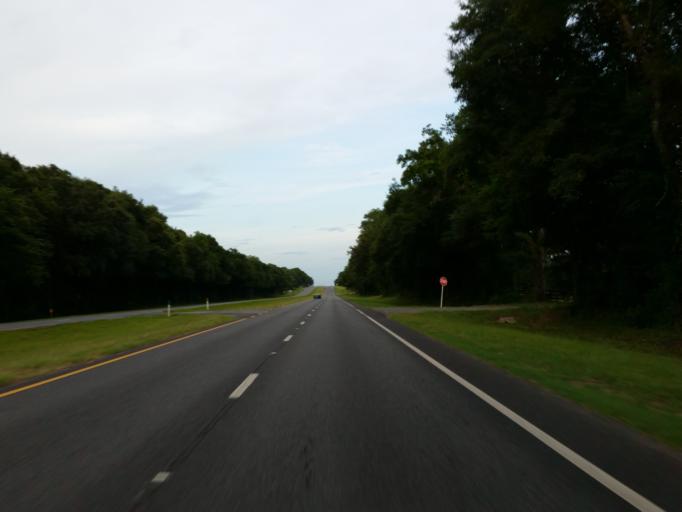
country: US
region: Florida
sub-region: Alachua County
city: High Springs
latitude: 29.8071
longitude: -82.5410
